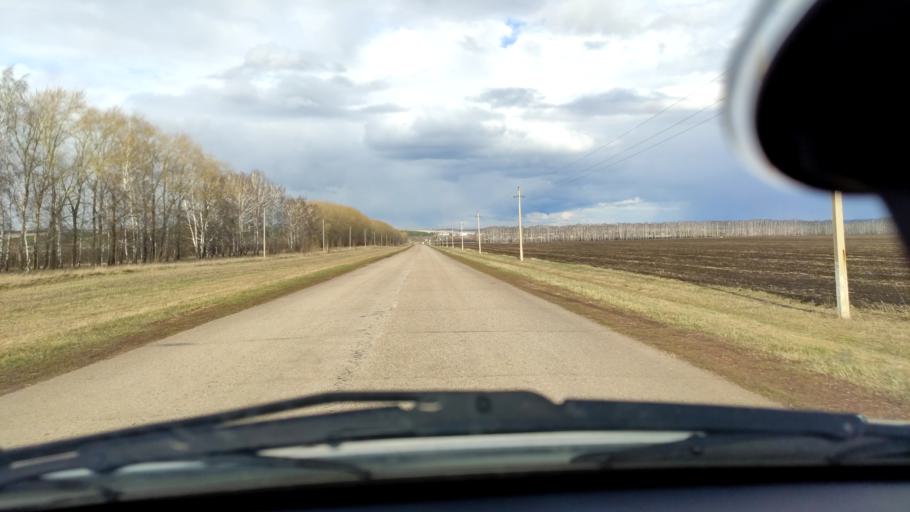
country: RU
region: Bashkortostan
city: Buzdyak
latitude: 54.7602
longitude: 54.5693
